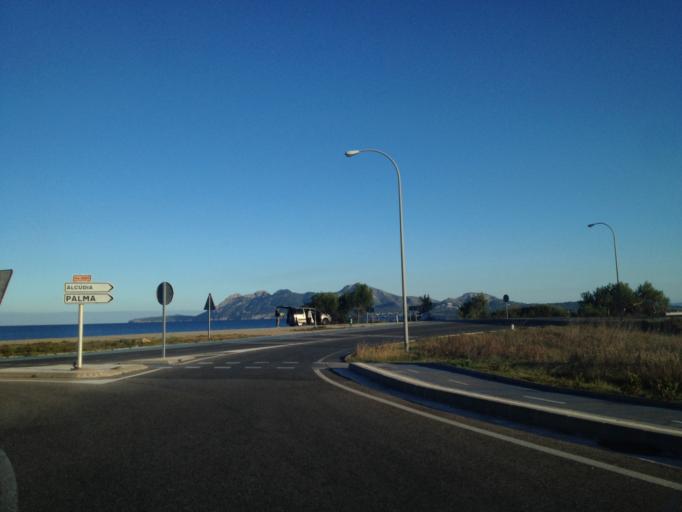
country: ES
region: Balearic Islands
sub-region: Illes Balears
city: Alcudia
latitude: 39.8835
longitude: 3.0792
